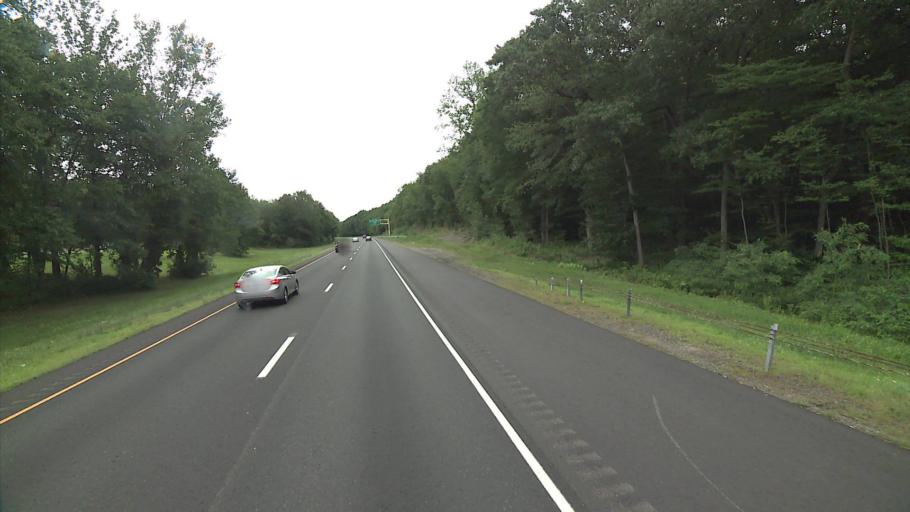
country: US
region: Connecticut
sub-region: Fairfield County
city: Shelton
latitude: 41.2618
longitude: -73.1332
